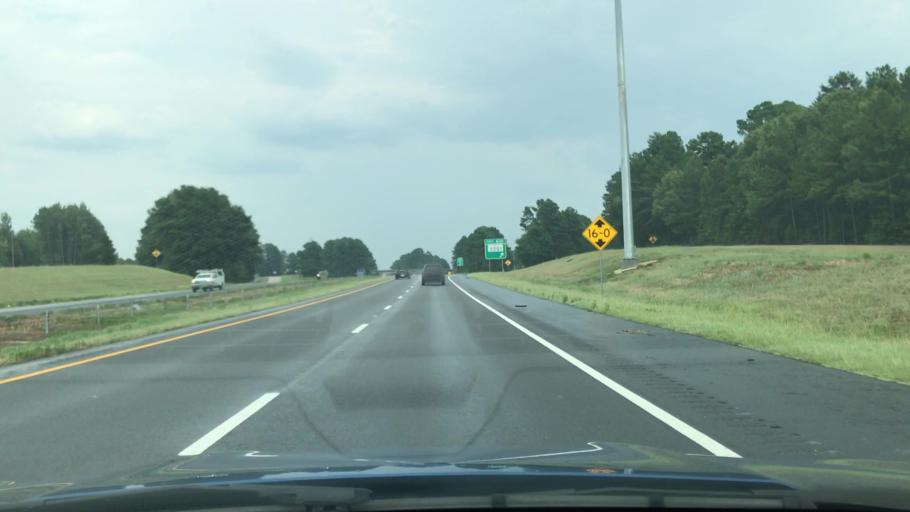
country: US
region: Texas
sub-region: Harrison County
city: Hallsville
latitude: 32.4862
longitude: -94.4747
